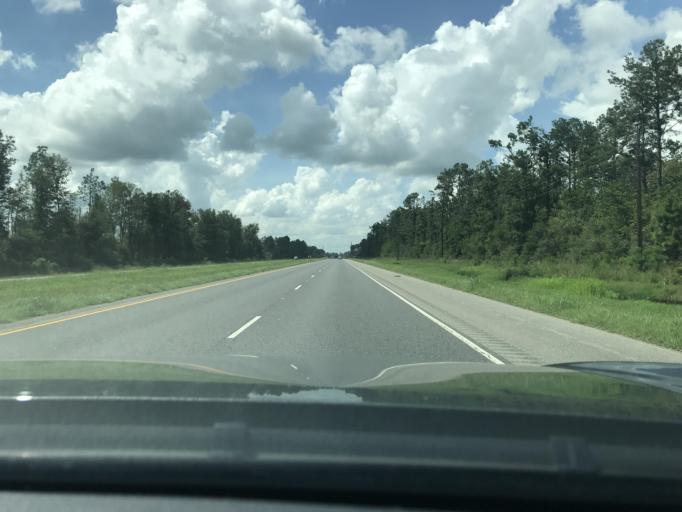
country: US
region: Louisiana
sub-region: Calcasieu Parish
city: Moss Bluff
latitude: 30.3427
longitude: -93.2004
